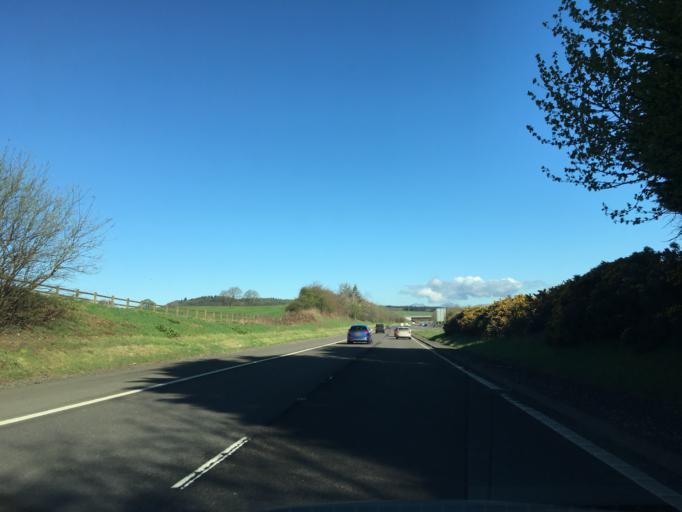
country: GB
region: Scotland
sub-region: Stirling
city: Bannockburn
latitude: 56.0829
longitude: -3.9390
